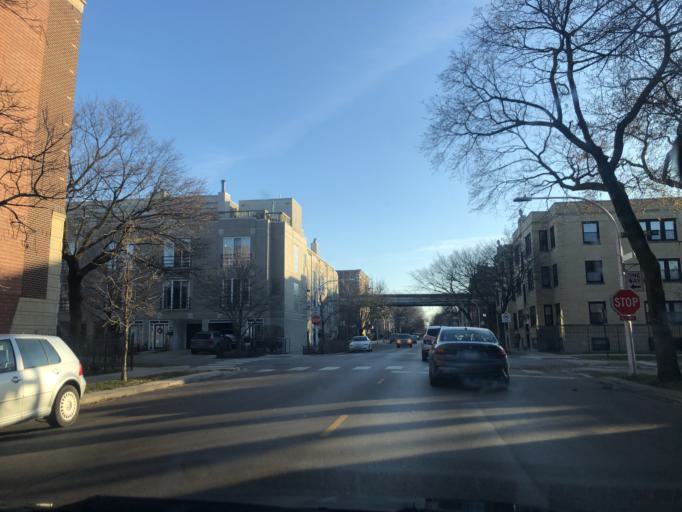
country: US
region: Illinois
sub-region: Cook County
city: Lincolnwood
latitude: 41.9448
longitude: -87.6591
